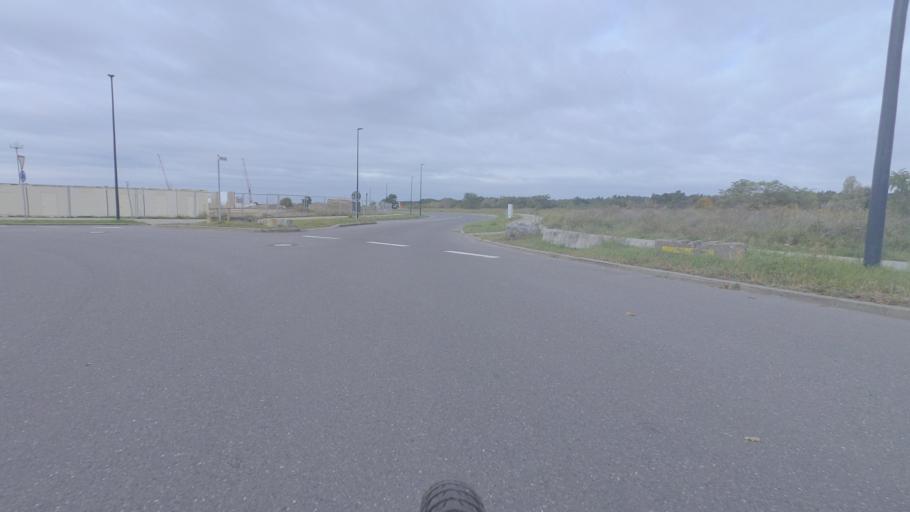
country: DE
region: Brandenburg
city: Grossbeeren
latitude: 52.3197
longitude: 13.3027
